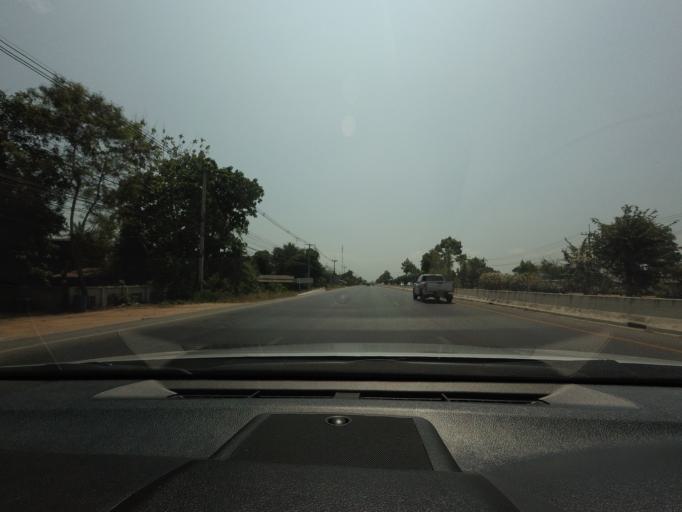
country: TH
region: Phetchaburi
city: Ban Lat
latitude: 13.0078
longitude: 99.9143
